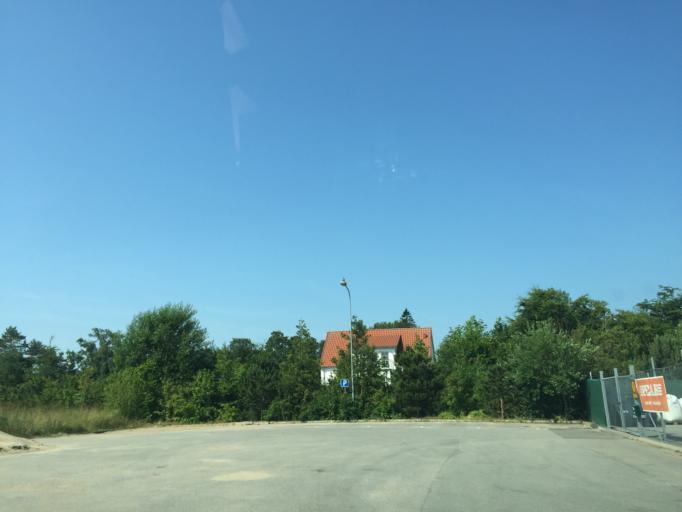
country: SE
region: Skane
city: Bjarred
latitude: 55.7393
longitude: 13.0326
